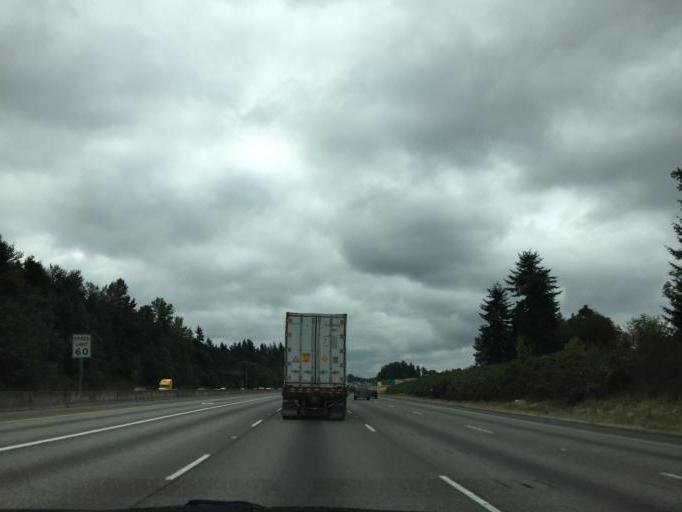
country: US
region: Washington
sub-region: King County
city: Des Moines
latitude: 47.3835
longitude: -122.2905
